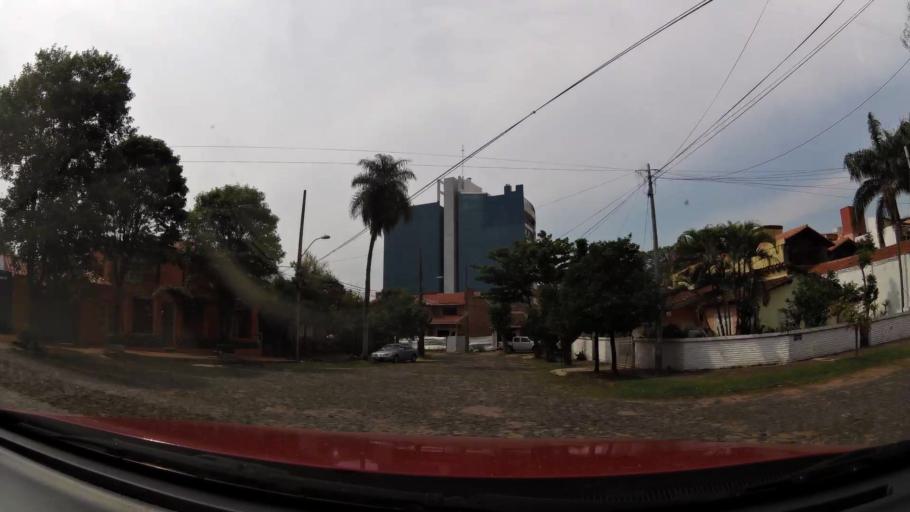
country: PY
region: Asuncion
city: Asuncion
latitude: -25.2781
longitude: -57.5686
